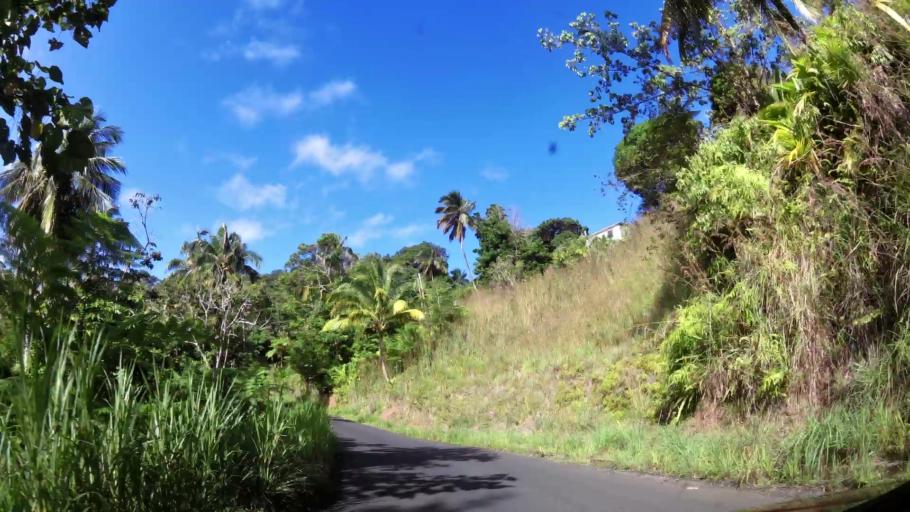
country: DM
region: Saint John
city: Portsmouth
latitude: 15.5798
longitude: -61.4191
